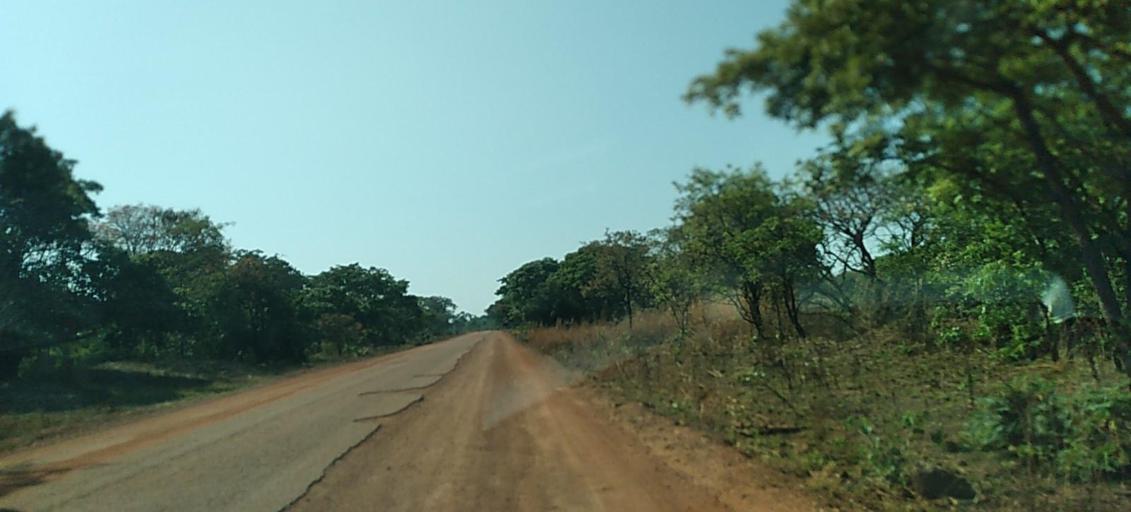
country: ZM
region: North-Western
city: Mwinilunga
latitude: -11.8969
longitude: 25.2734
